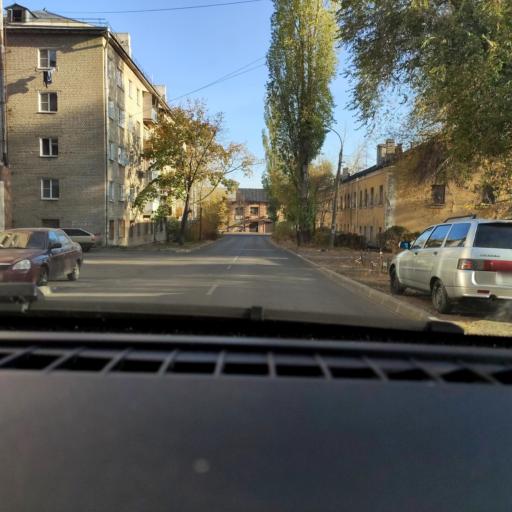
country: RU
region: Voronezj
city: Maslovka
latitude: 51.6192
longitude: 39.2470
